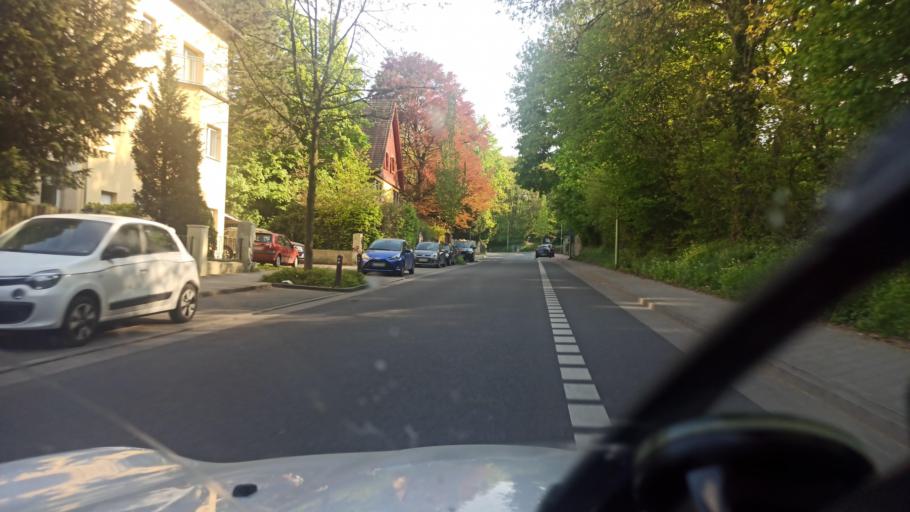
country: DE
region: North Rhine-Westphalia
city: Stolberg
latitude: 50.7628
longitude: 6.2283
